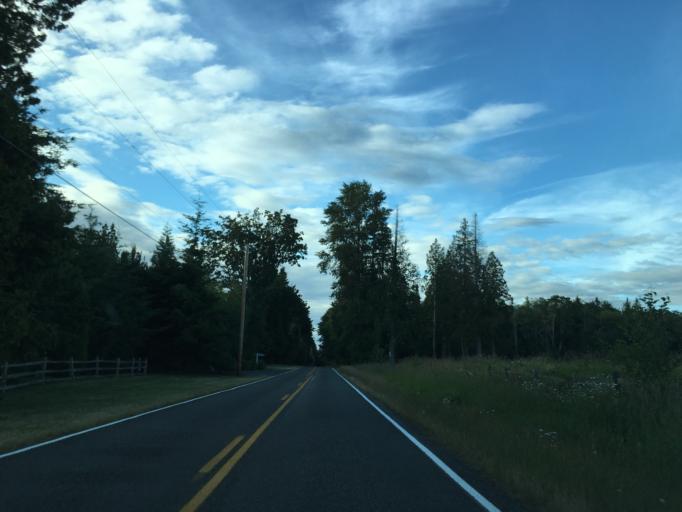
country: CA
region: British Columbia
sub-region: Greater Vancouver Regional District
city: White Rock
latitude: 48.9490
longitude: -122.8180
